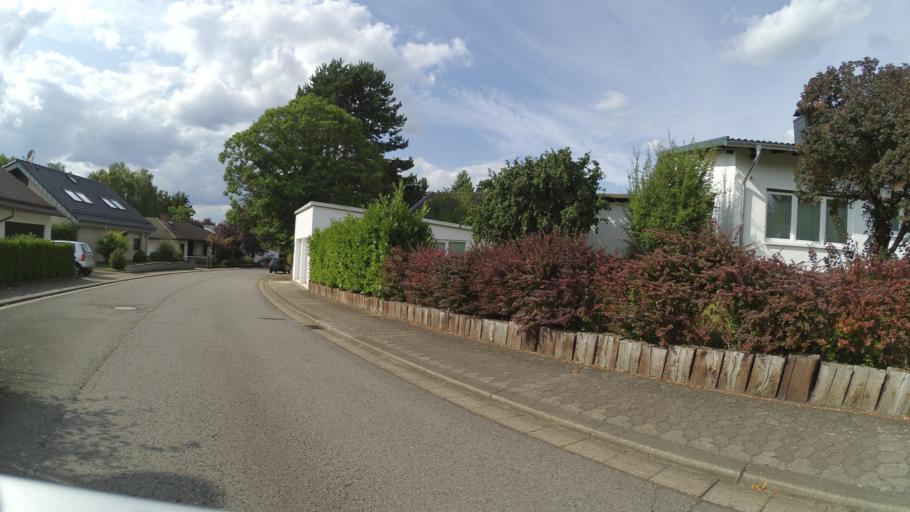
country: DE
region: Saarland
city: Bexbach
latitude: 49.3053
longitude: 7.2740
